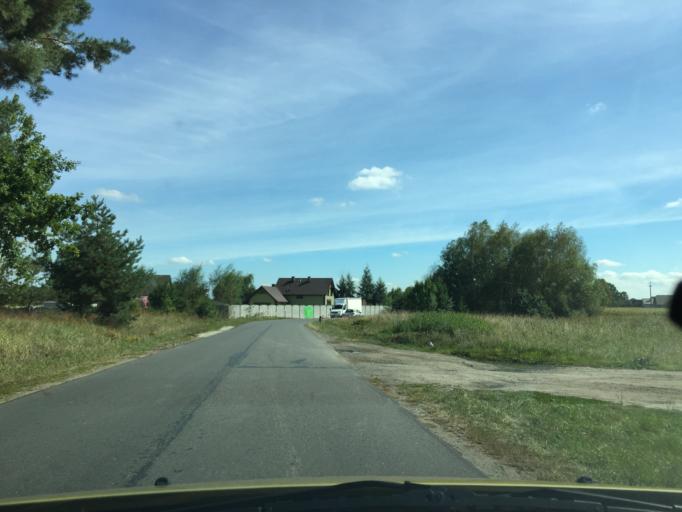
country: PL
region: Greater Poland Voivodeship
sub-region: Powiat kaliski
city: Stawiszyn
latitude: 51.9479
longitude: 18.1795
